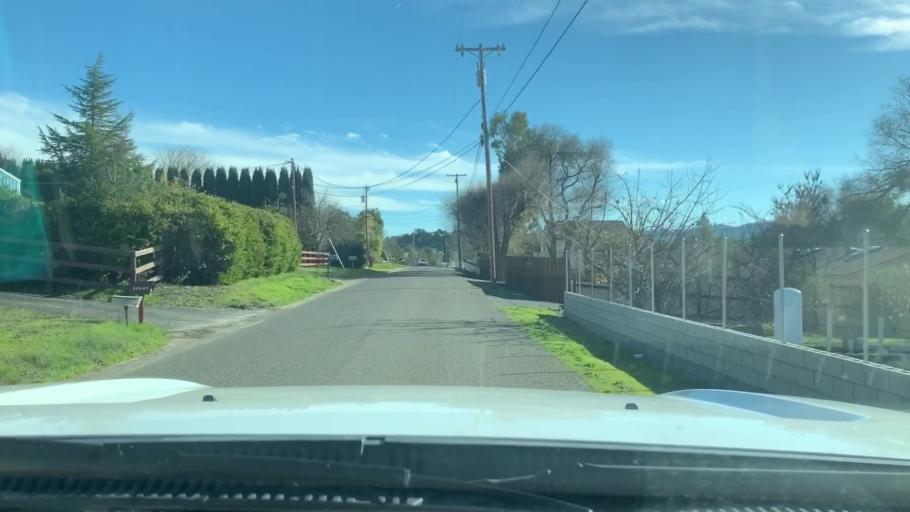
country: US
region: California
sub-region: San Luis Obispo County
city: Santa Margarita
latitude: 35.4364
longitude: -120.6346
